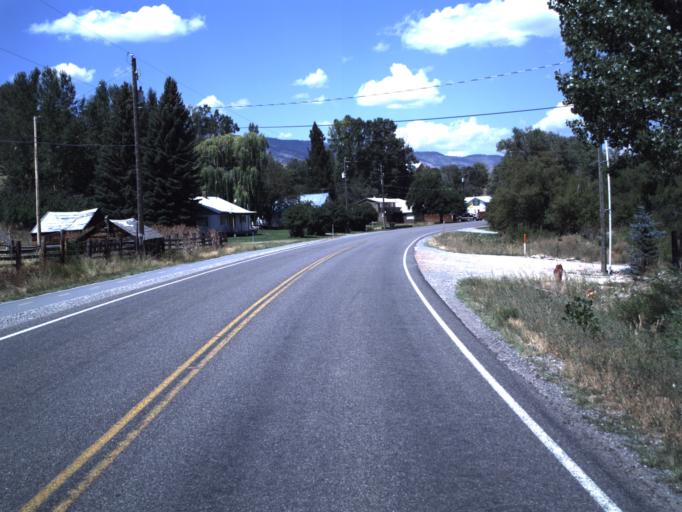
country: US
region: Idaho
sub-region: Bear Lake County
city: Paris
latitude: 41.9223
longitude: -111.3960
